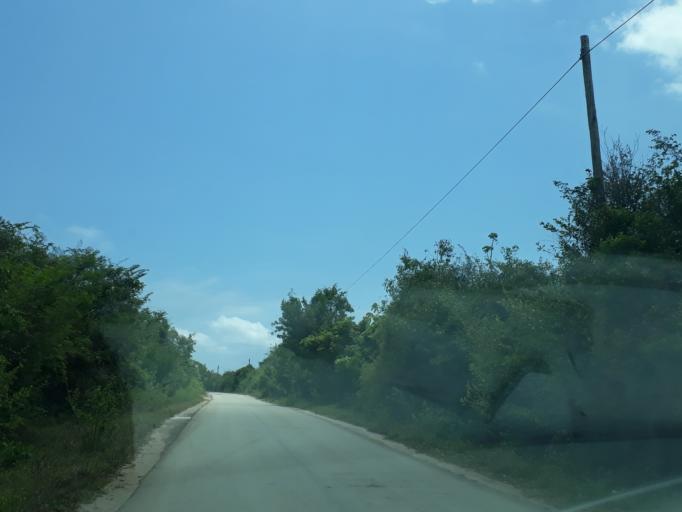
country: TZ
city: Kiwengwa
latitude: -5.9922
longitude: 39.3683
